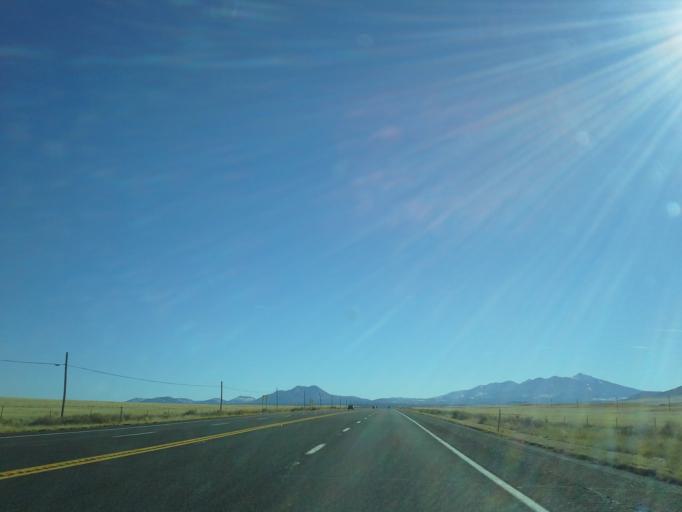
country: US
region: Arizona
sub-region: Coconino County
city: Flagstaff
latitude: 35.6326
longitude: -111.5197
